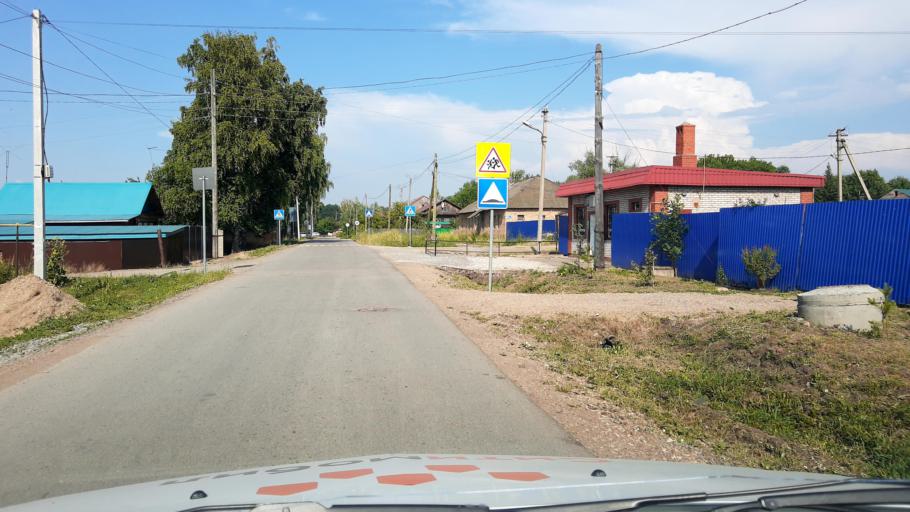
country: RU
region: Bashkortostan
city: Iglino
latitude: 54.8319
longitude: 56.3939
